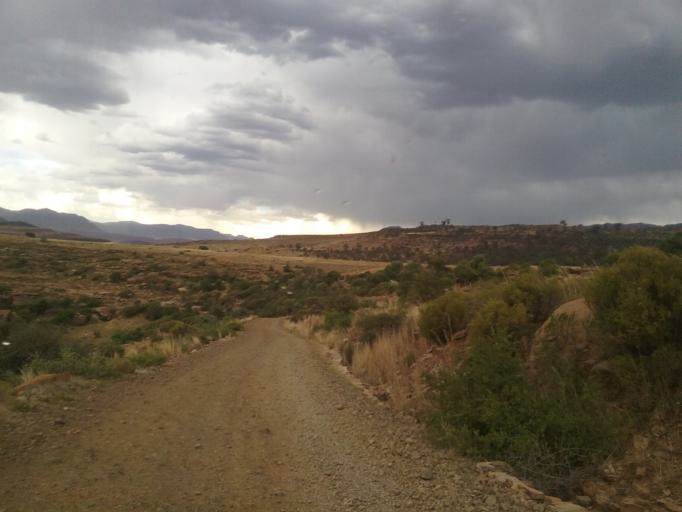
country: LS
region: Quthing
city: Quthing
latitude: -30.3047
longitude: 27.8135
